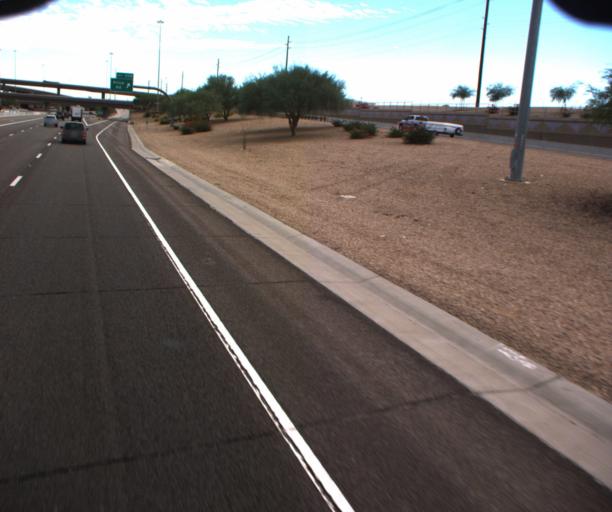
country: US
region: Arizona
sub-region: Maricopa County
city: Chandler
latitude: 33.2919
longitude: -111.8993
